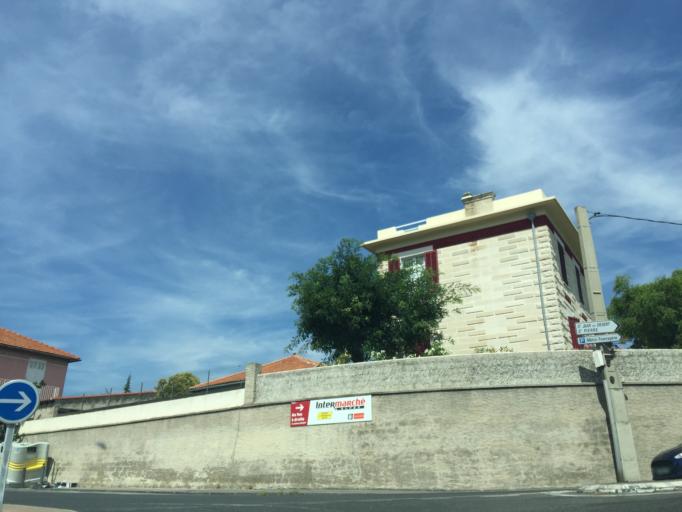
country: FR
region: Provence-Alpes-Cote d'Azur
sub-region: Departement des Bouches-du-Rhone
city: Marseille 04
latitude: 43.2982
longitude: 5.4167
